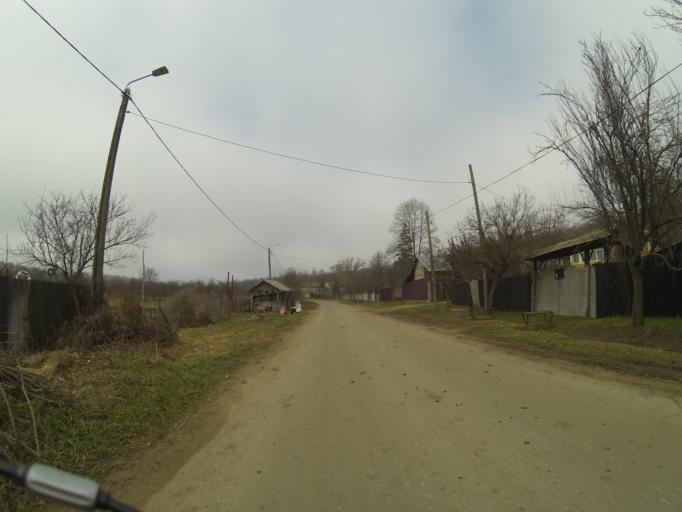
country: RO
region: Mehedinti
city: Padina Mica
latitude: 44.4911
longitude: 23.0082
